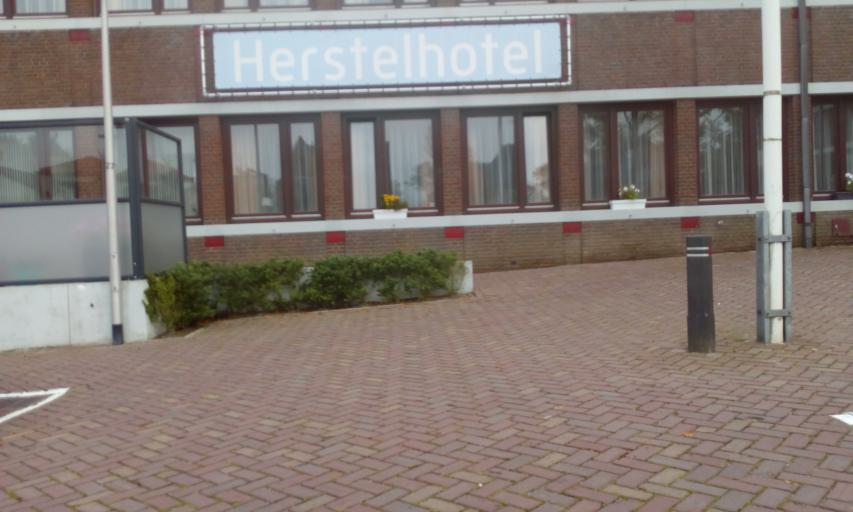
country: NL
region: South Holland
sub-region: Gemeente Lansingerland
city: Bleiswijk
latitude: 52.0089
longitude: 4.5297
